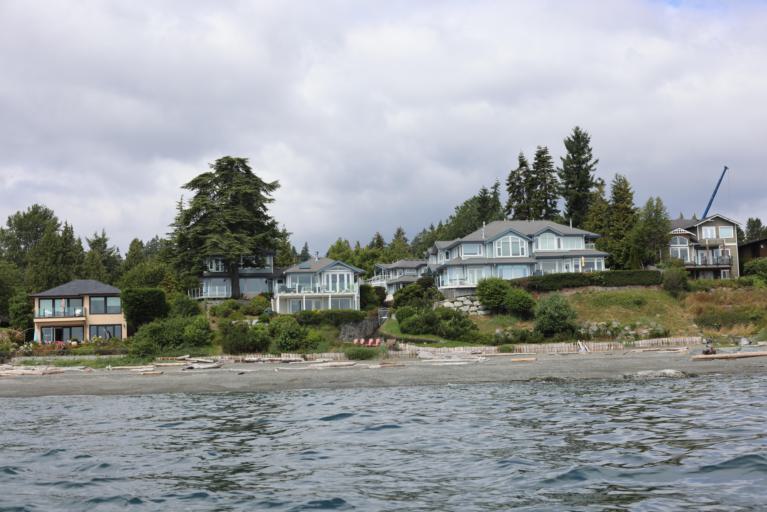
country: CA
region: British Columbia
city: Victoria
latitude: 48.5251
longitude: -123.3639
